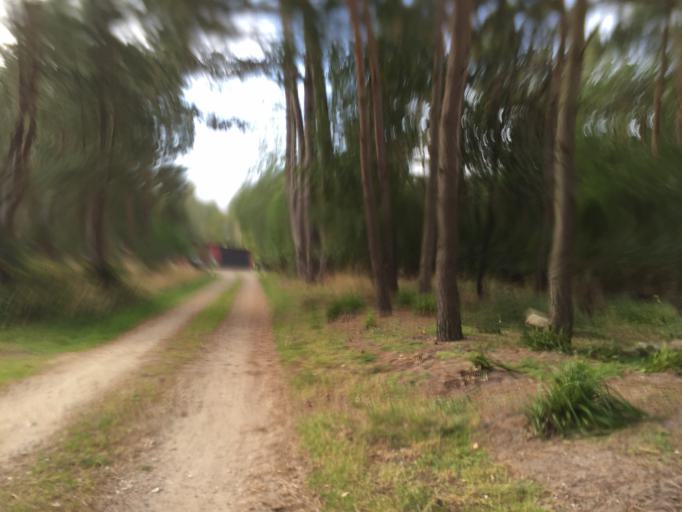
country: DK
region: Zealand
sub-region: Odsherred Kommune
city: Hojby
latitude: 55.8996
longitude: 11.5583
